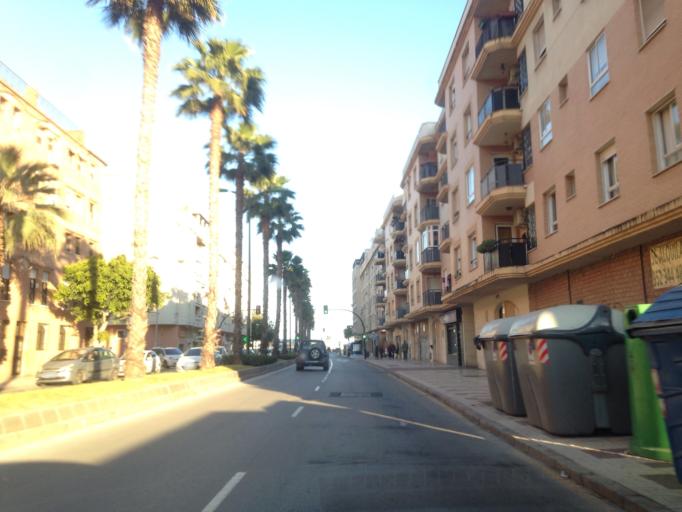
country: ES
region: Andalusia
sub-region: Provincia de Malaga
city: Malaga
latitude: 36.6860
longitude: -4.4514
